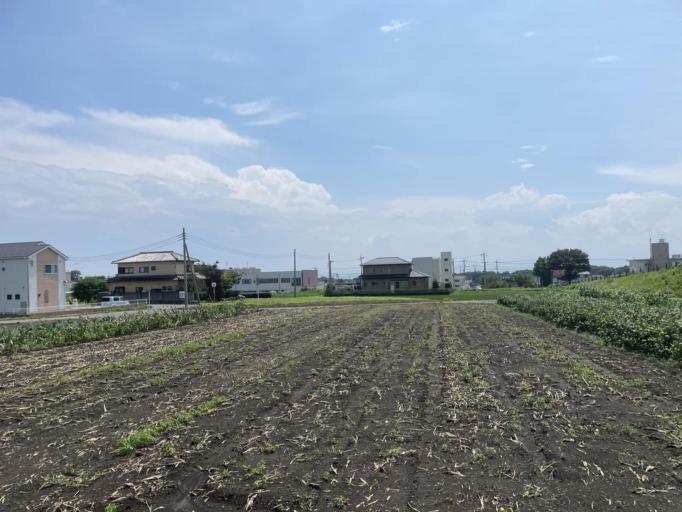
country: JP
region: Gunma
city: Omamacho-omama
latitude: 36.4146
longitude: 139.1790
